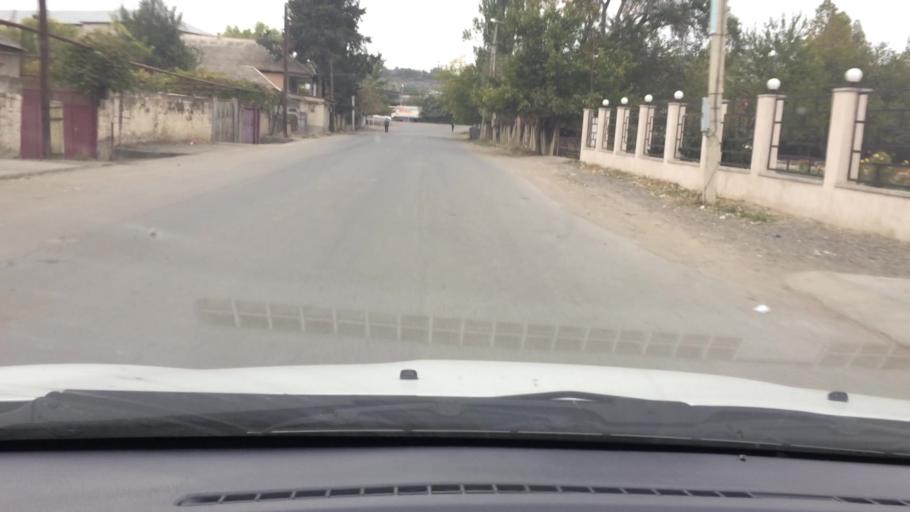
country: GE
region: Kvemo Kartli
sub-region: Marneuli
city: Marneuli
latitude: 41.4825
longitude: 44.7944
